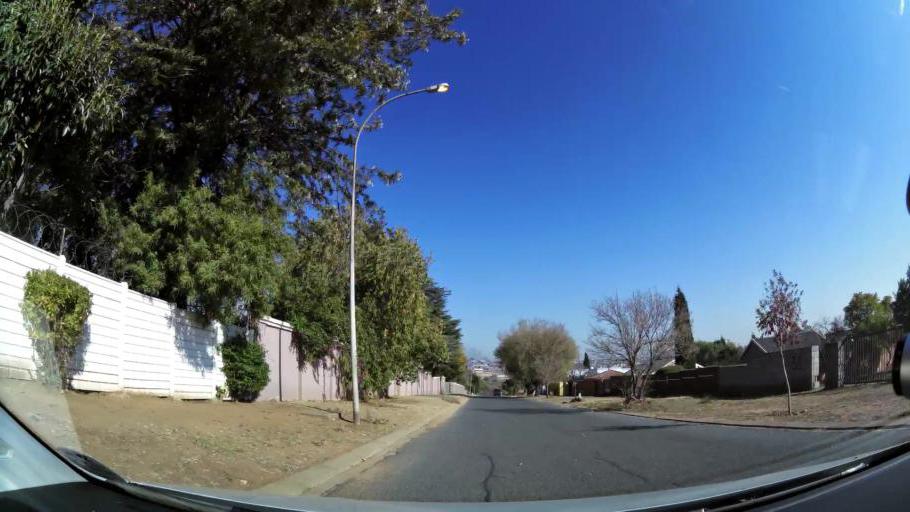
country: ZA
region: Gauteng
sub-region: City of Johannesburg Metropolitan Municipality
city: Modderfontein
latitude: -26.1127
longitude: 28.1199
